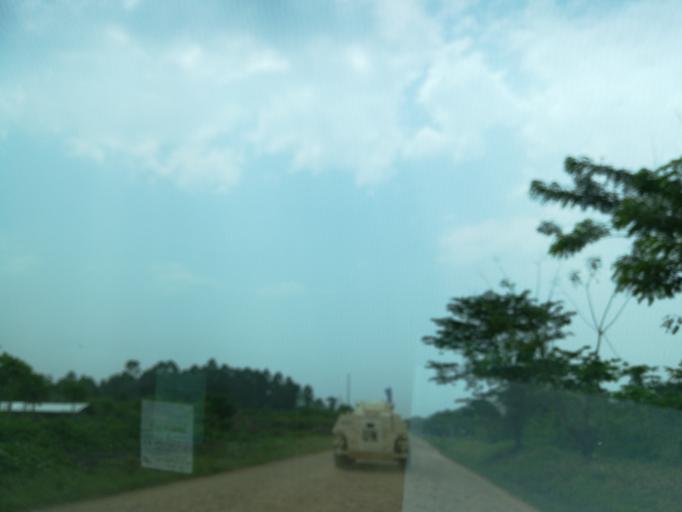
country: UG
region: Western Region
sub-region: Kasese District
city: Margherita
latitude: 0.3119
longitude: 29.6708
